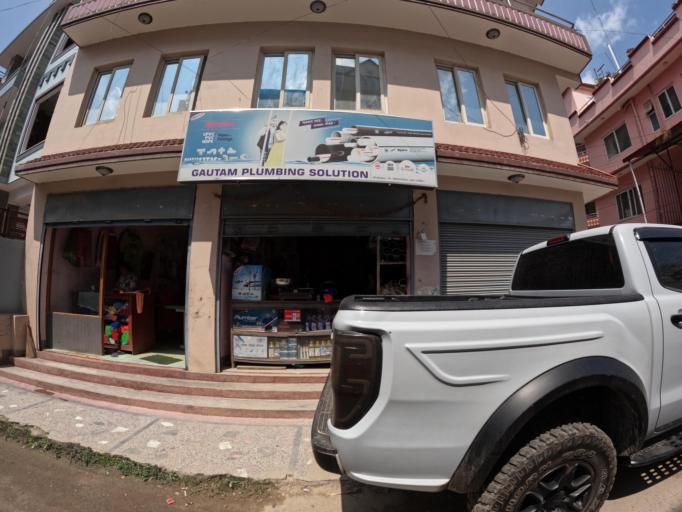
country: NP
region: Central Region
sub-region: Bagmati Zone
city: Patan
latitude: 27.6704
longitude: 85.3585
